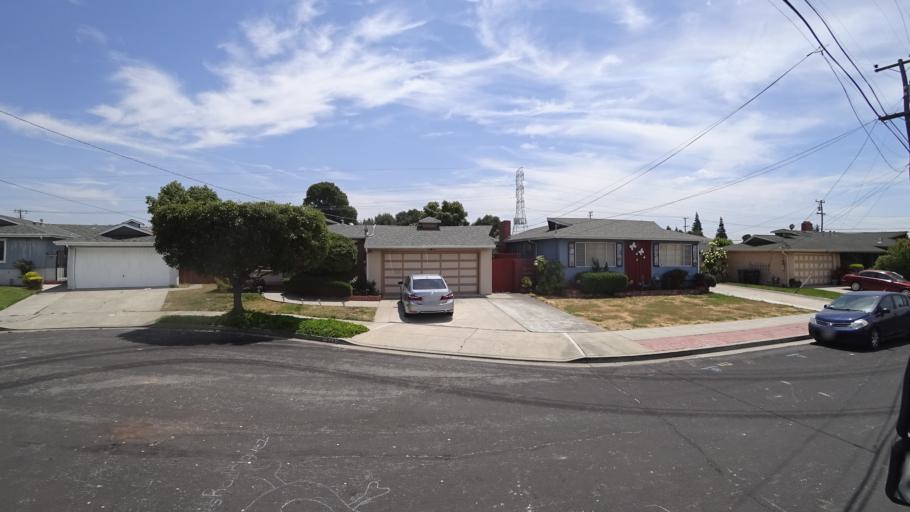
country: US
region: California
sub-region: Alameda County
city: Hayward
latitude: 37.6463
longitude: -122.0886
